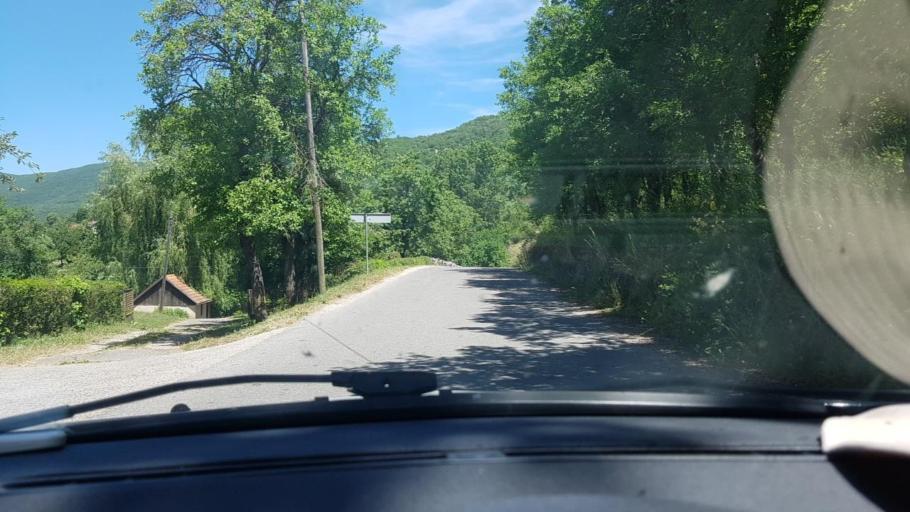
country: HR
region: Licko-Senjska
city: Otocac
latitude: 44.7884
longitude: 15.3681
